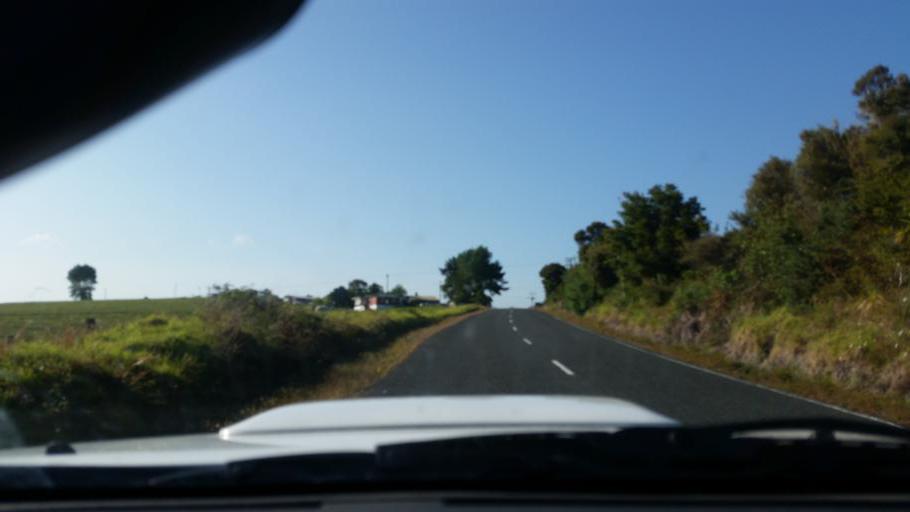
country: NZ
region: Northland
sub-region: Whangarei
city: Ruakaka
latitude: -36.1188
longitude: 174.2322
